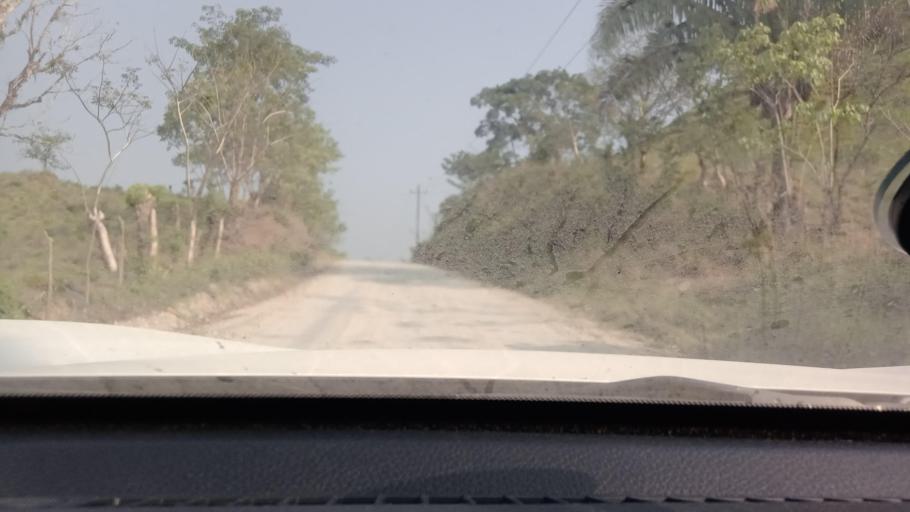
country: MX
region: Tabasco
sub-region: Huimanguillo
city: Francisco Rueda
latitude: 17.6163
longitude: -93.9401
